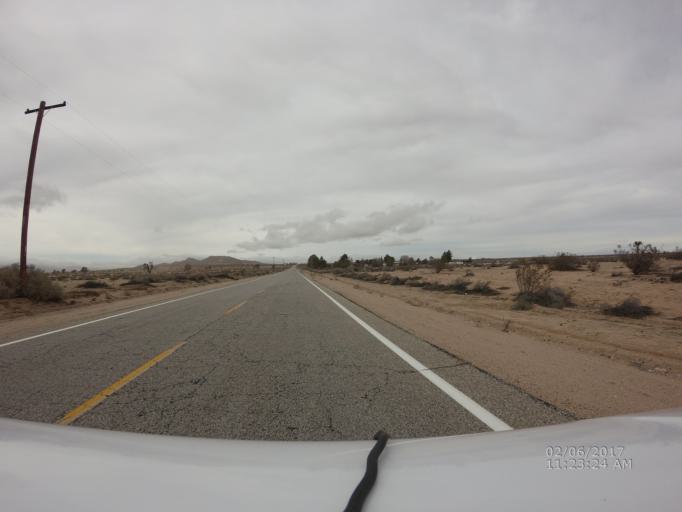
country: US
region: California
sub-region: Los Angeles County
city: Lake Los Angeles
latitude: 34.6899
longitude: -117.7403
